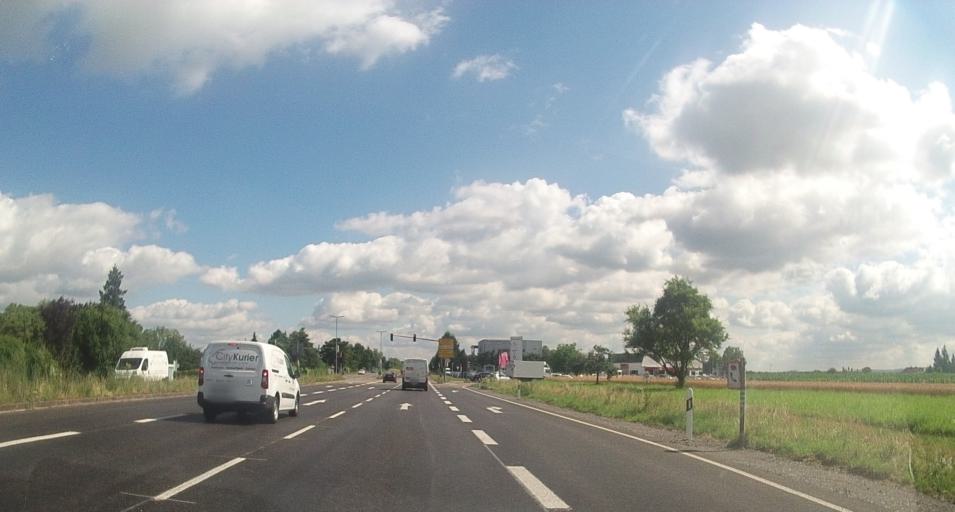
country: DE
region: Baden-Wuerttemberg
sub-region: Karlsruhe Region
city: Rheinstetten
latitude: 48.9574
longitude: 8.2969
